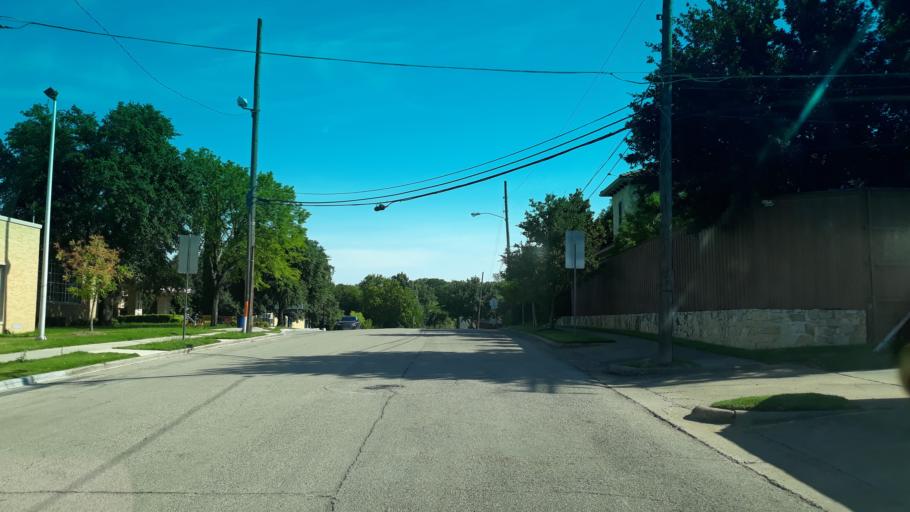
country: US
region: Texas
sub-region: Dallas County
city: Highland Park
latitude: 32.8264
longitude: -96.7444
